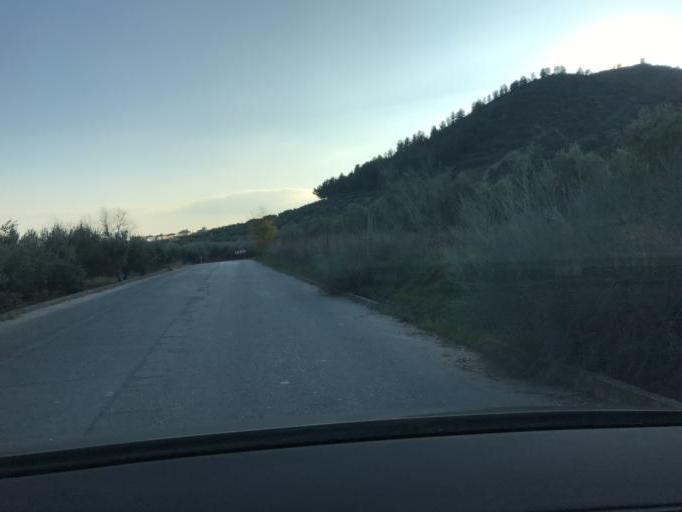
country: ES
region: Andalusia
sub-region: Provincia de Granada
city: Albolote
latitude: 37.2515
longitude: -3.6731
